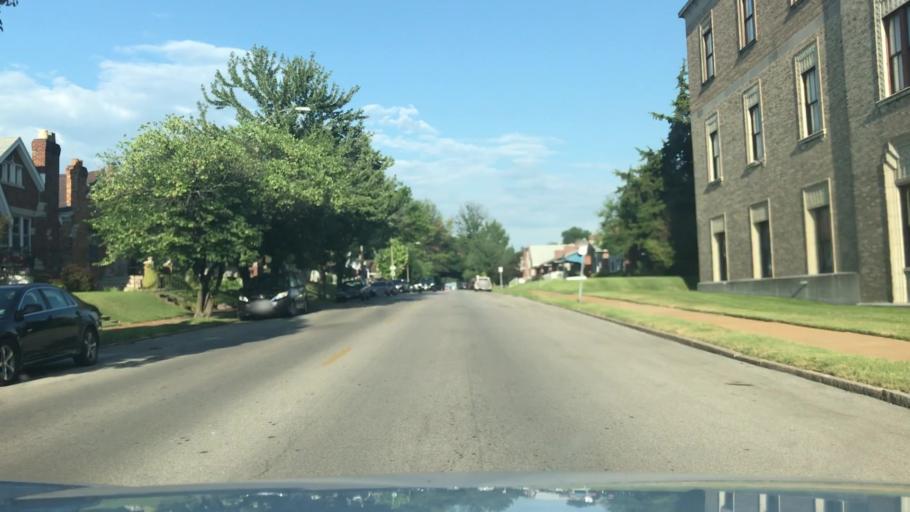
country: US
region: Missouri
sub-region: Saint Louis County
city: Maplewood
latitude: 38.5820
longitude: -90.2889
